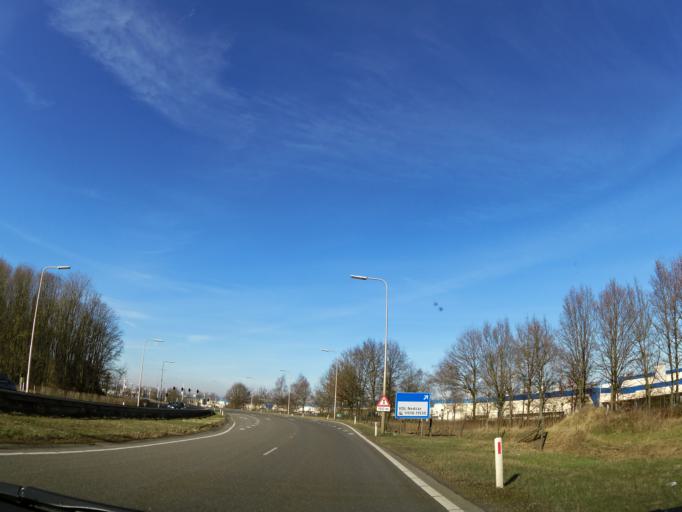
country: NL
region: Limburg
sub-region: Gemeente Sittard-Geleen
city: Limbricht
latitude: 51.0377
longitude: 5.8374
